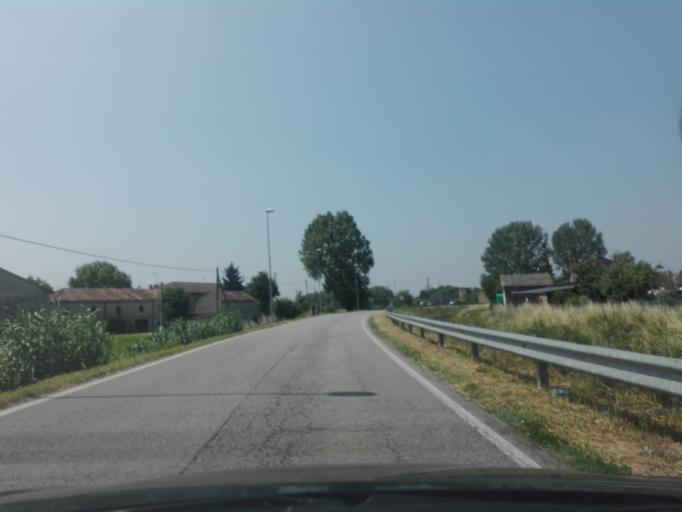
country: IT
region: Veneto
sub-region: Provincia di Rovigo
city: Ceregnano
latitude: 45.0646
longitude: 11.8712
